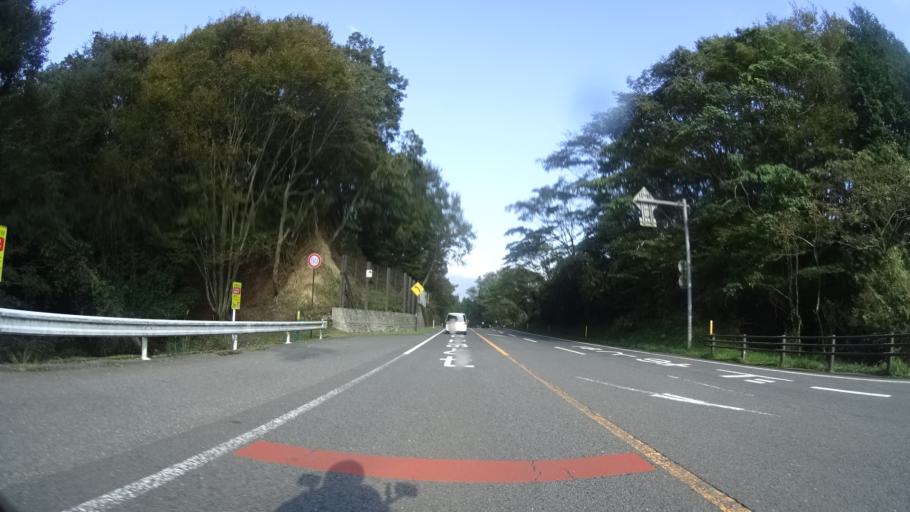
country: JP
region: Oita
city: Tsukawaki
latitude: 33.2533
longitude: 131.3063
